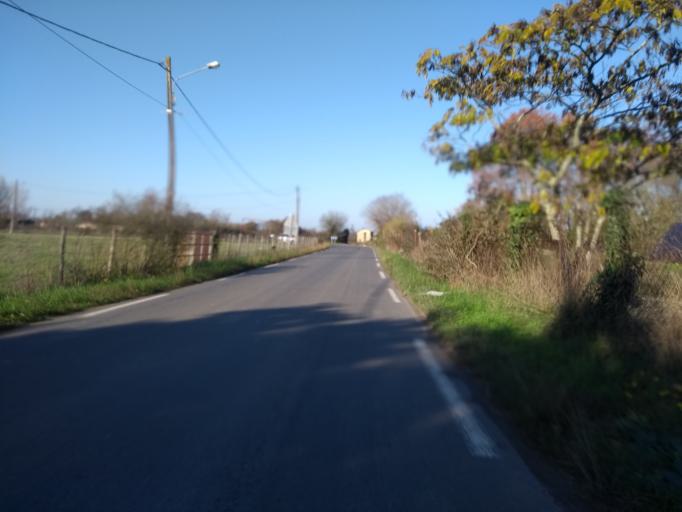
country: FR
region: Aquitaine
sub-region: Departement de la Gironde
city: Martillac
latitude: 44.7276
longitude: -0.5118
